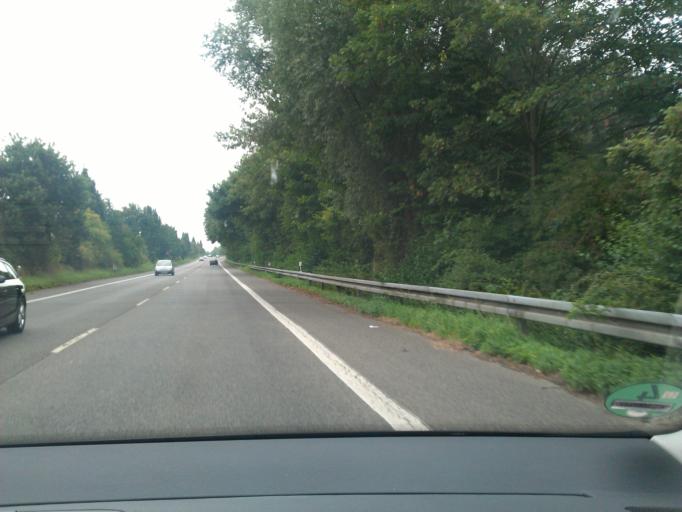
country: DE
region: North Rhine-Westphalia
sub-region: Regierungsbezirk Dusseldorf
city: Hilden
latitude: 51.1791
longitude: 6.9476
